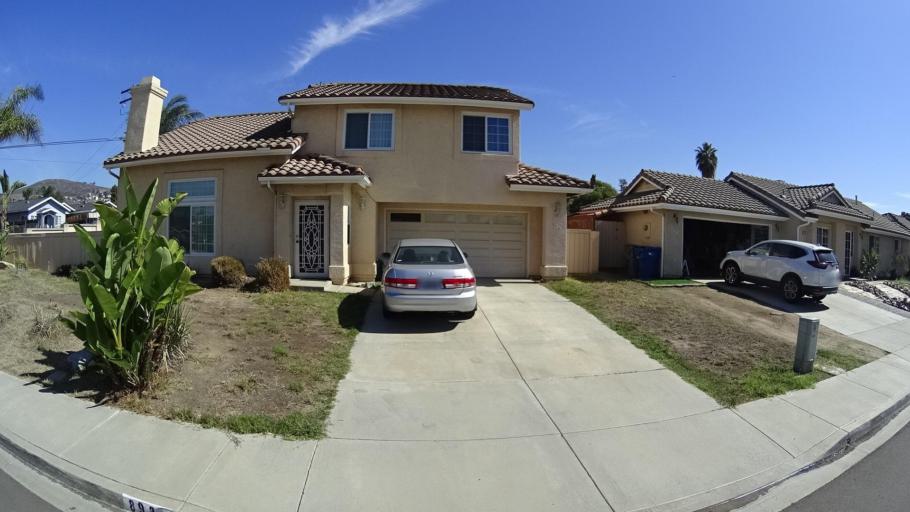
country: US
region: California
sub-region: San Diego County
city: La Presa
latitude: 32.7119
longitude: -117.0085
